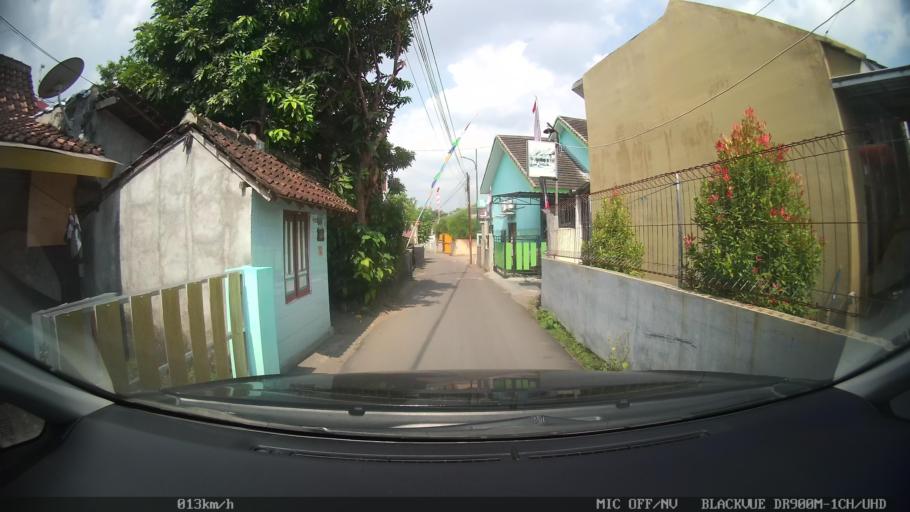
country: ID
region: Daerah Istimewa Yogyakarta
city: Yogyakarta
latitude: -7.8204
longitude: 110.3974
